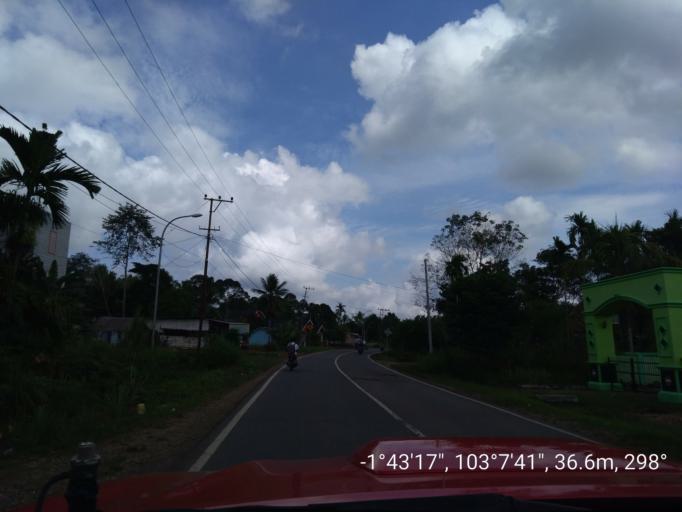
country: ID
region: Jambi
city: Muara Tembesi
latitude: -1.7214
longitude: 103.1283
